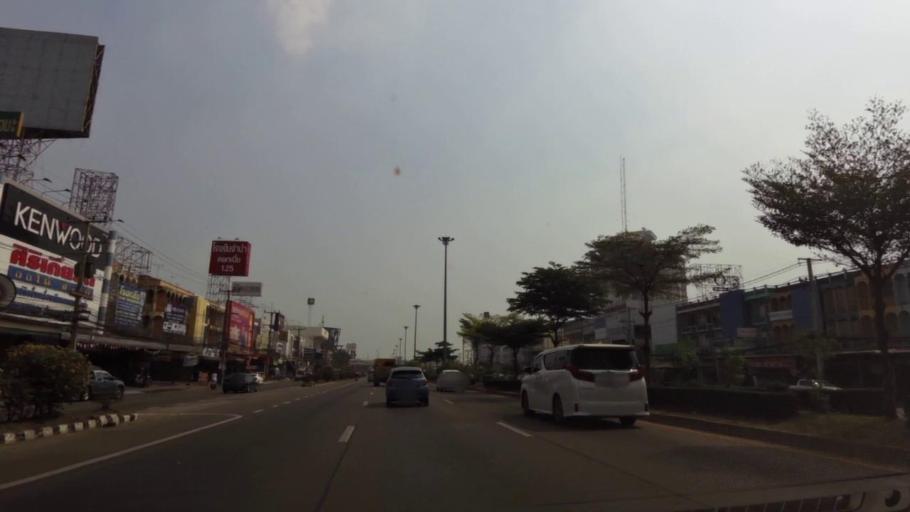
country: TH
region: Phra Nakhon Si Ayutthaya
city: Phra Nakhon Si Ayutthaya
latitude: 14.3471
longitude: 100.6063
